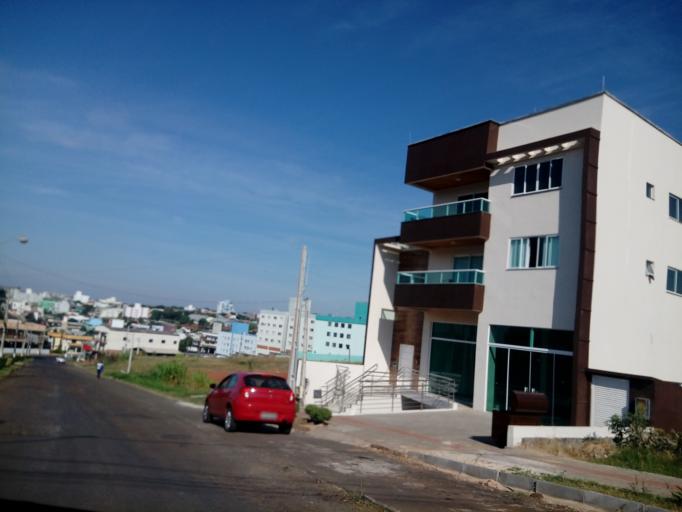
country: BR
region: Santa Catarina
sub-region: Chapeco
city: Chapeco
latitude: -27.0942
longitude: -52.6666
